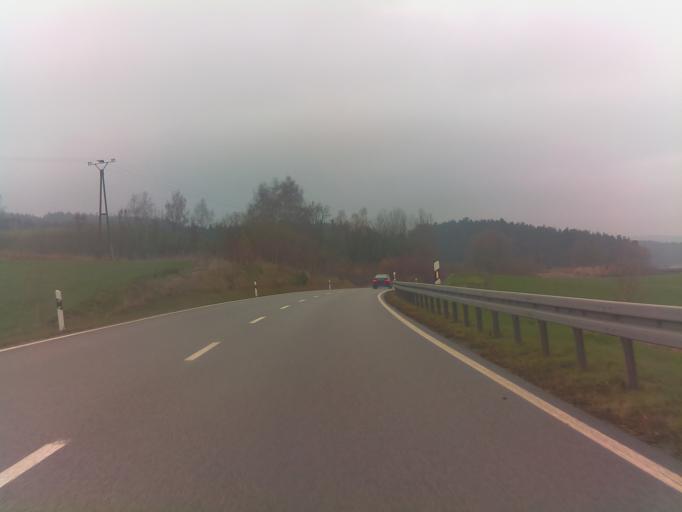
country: DE
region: Thuringia
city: Schleusingen
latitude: 50.4973
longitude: 10.7524
